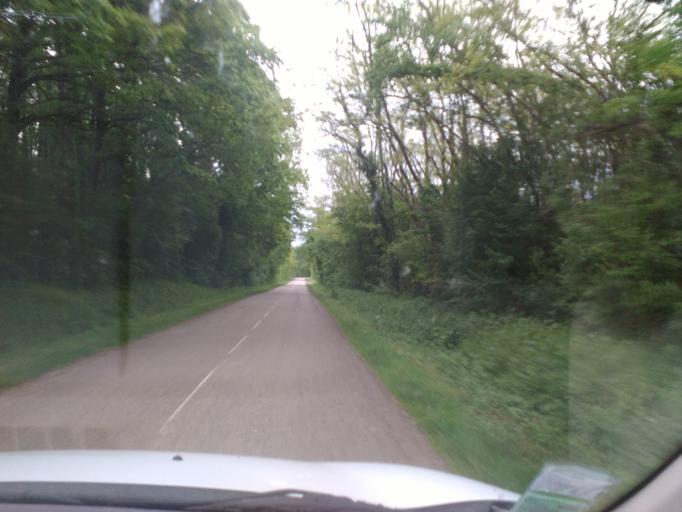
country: FR
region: Bourgogne
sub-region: Departement de l'Yonne
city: Thorigny-sur-Oreuse
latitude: 48.3573
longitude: 3.4274
